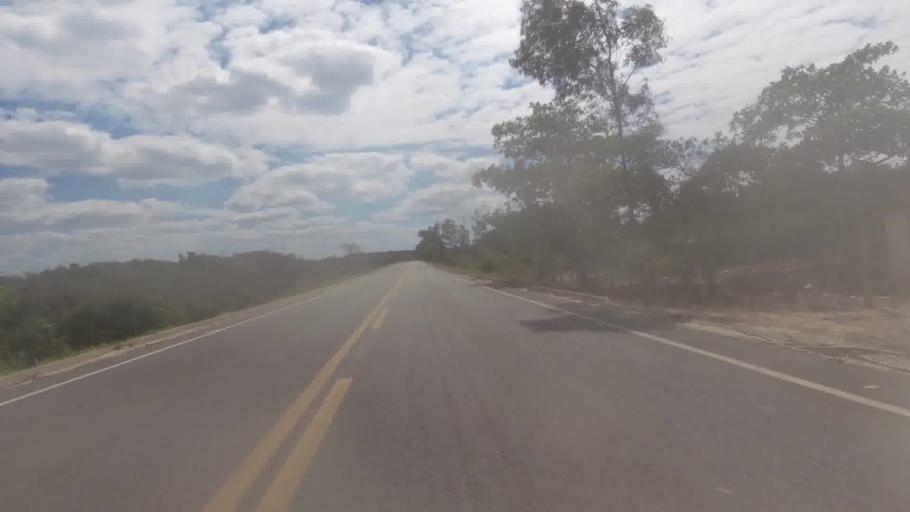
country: BR
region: Espirito Santo
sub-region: Marataizes
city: Marataizes
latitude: -21.2133
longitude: -40.9652
